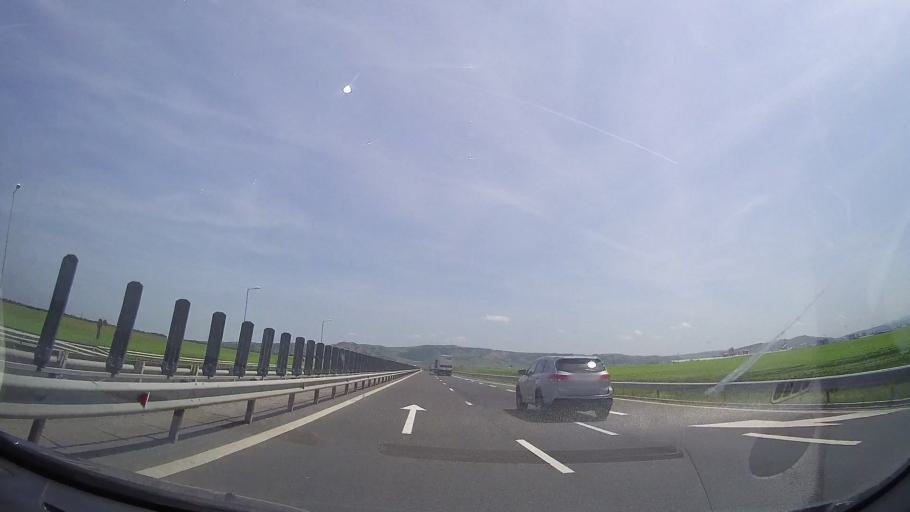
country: RO
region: Alba
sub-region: Municipiul Sebes
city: Lancram
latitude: 45.9786
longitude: 23.5258
